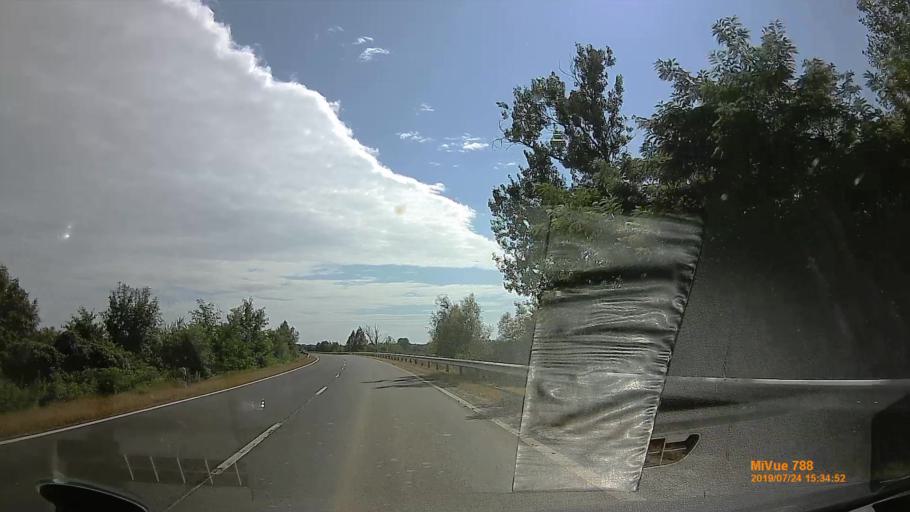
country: HU
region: Szabolcs-Szatmar-Bereg
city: Vasarosnameny
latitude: 48.1457
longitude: 22.3632
